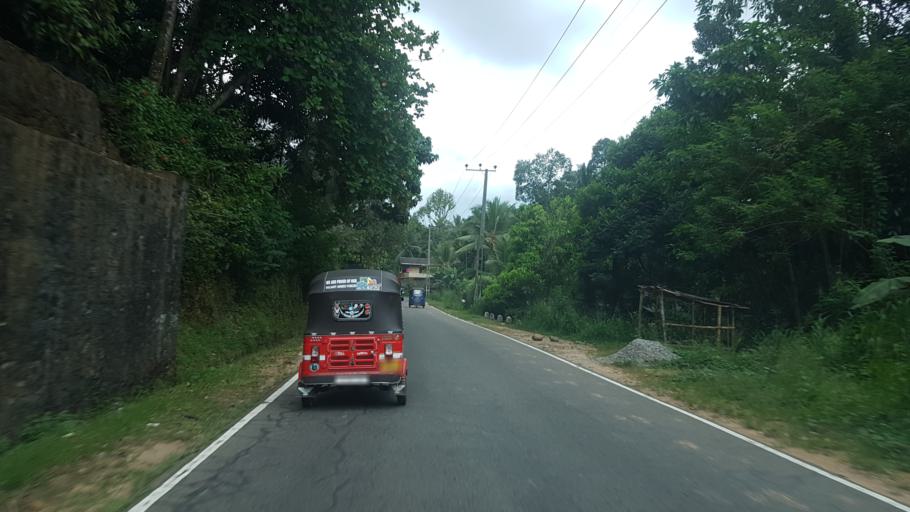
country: LK
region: Western
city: Hanwella Ihala
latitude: 7.0268
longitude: 80.2779
